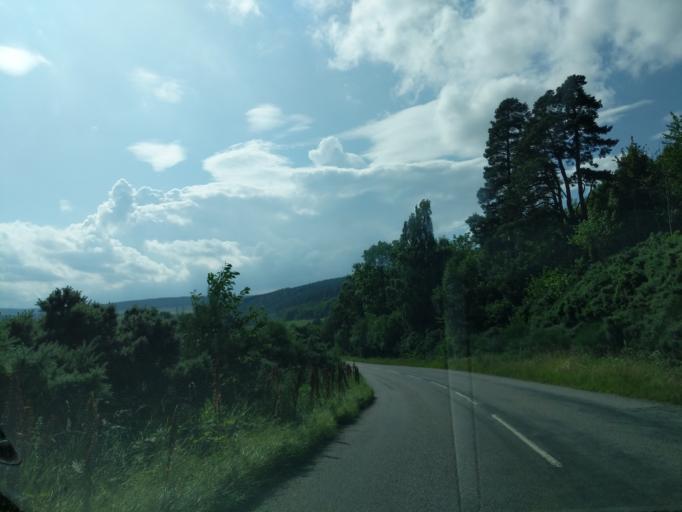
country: GB
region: Scotland
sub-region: Moray
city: Rothes
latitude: 57.5427
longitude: -3.1792
